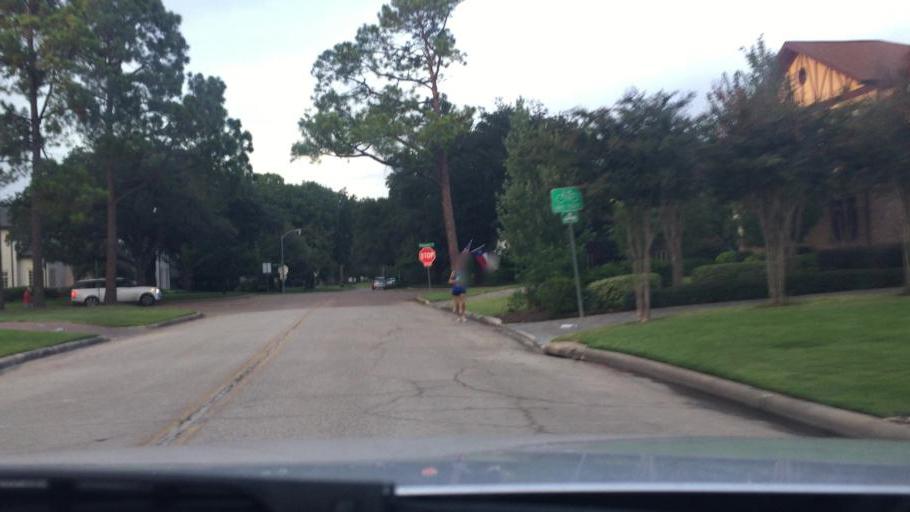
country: US
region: Texas
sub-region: Harris County
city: Hunters Creek Village
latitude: 29.7578
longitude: -95.4740
